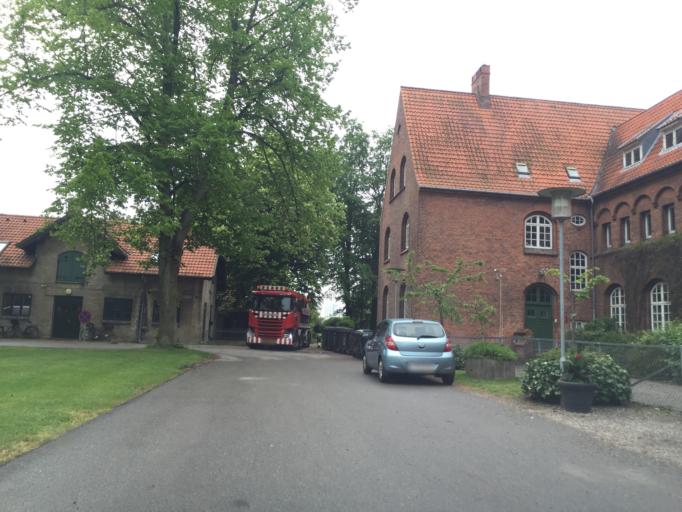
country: DK
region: Capital Region
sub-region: Rodovre Kommune
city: Rodovre
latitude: 55.6775
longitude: 12.4405
